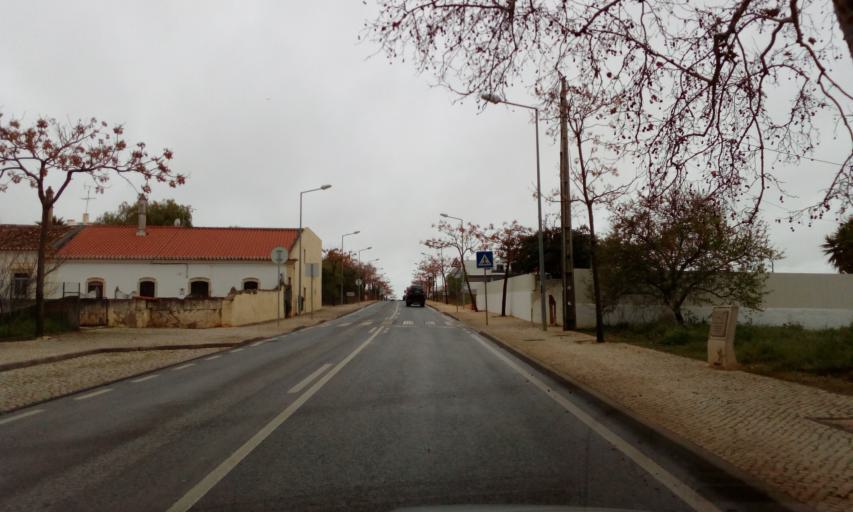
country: PT
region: Faro
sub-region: Albufeira
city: Ferreiras
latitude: 37.1275
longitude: -8.2463
